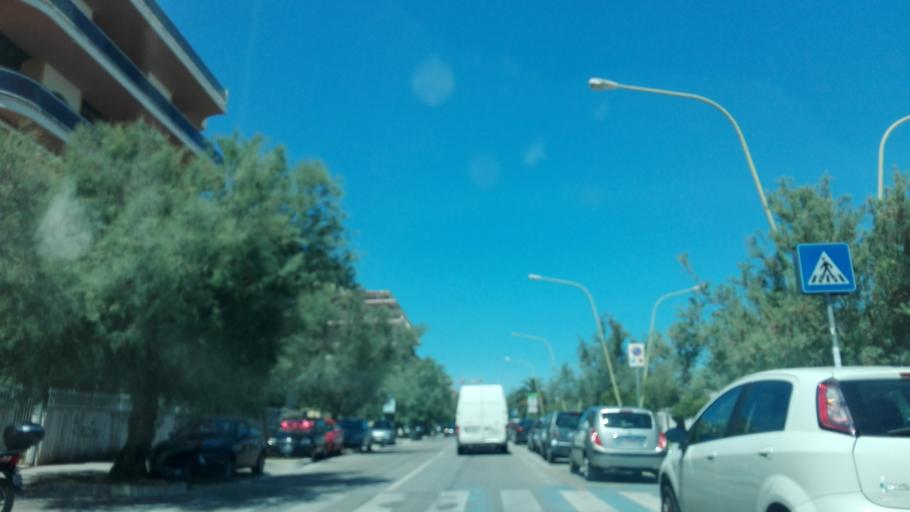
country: IT
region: Abruzzo
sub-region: Provincia di Pescara
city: Pescara
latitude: 42.4780
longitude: 14.2046
